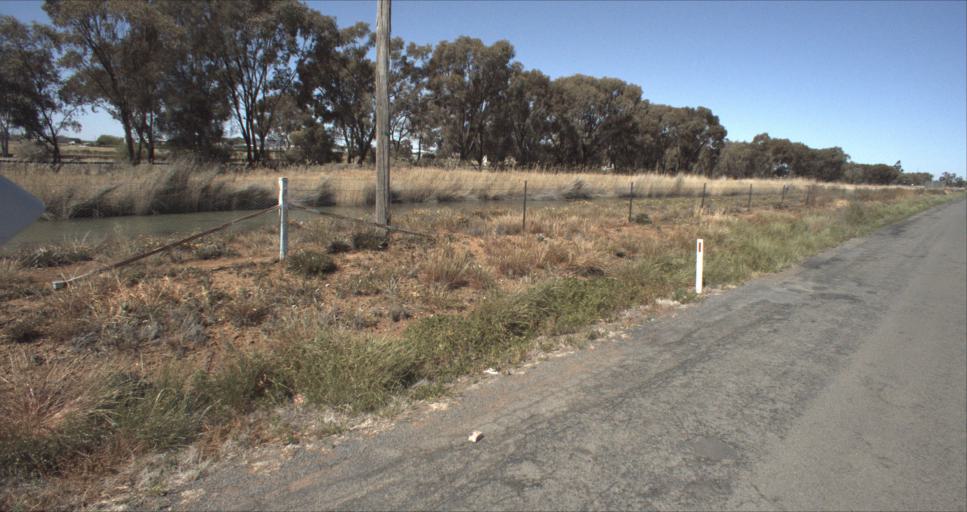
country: AU
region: New South Wales
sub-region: Leeton
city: Leeton
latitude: -34.5489
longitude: 146.3801
